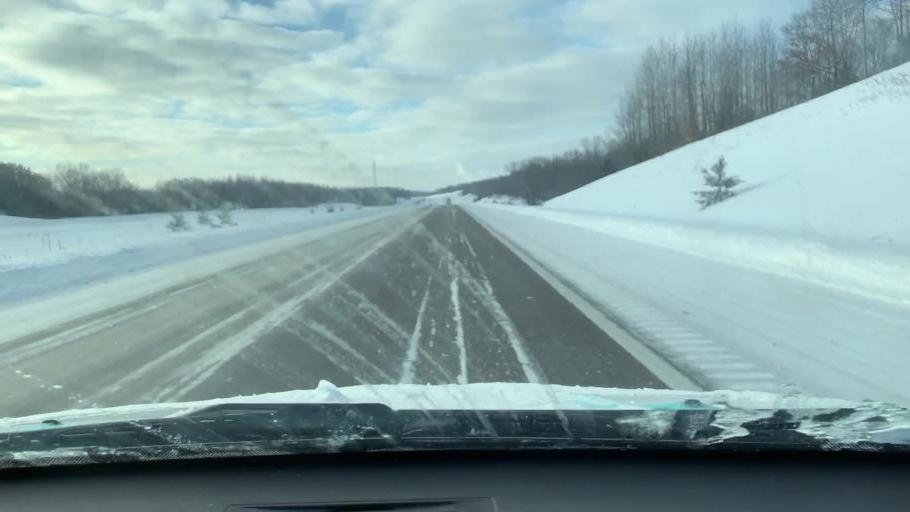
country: US
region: Michigan
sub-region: Wexford County
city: Manton
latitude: 44.3489
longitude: -85.4047
